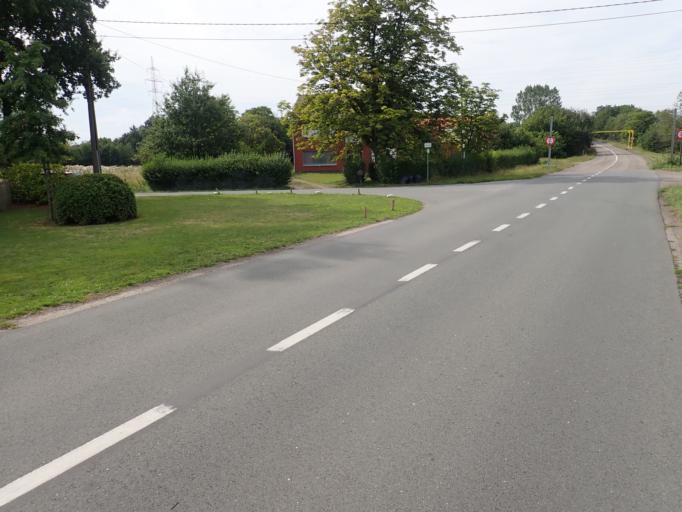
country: BE
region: Flanders
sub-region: Provincie Antwerpen
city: Zandhoven
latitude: 51.2204
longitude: 4.6501
